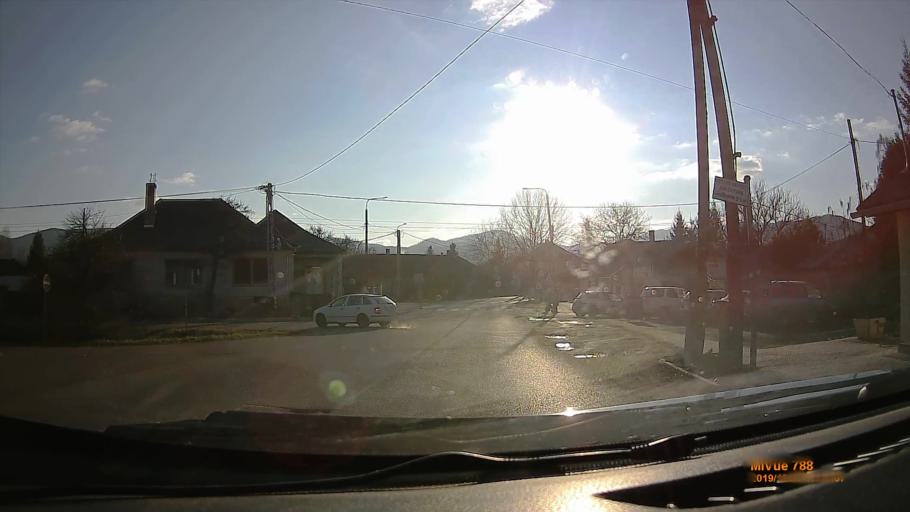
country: HU
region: Heves
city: Recsk
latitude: 47.9315
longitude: 20.1040
